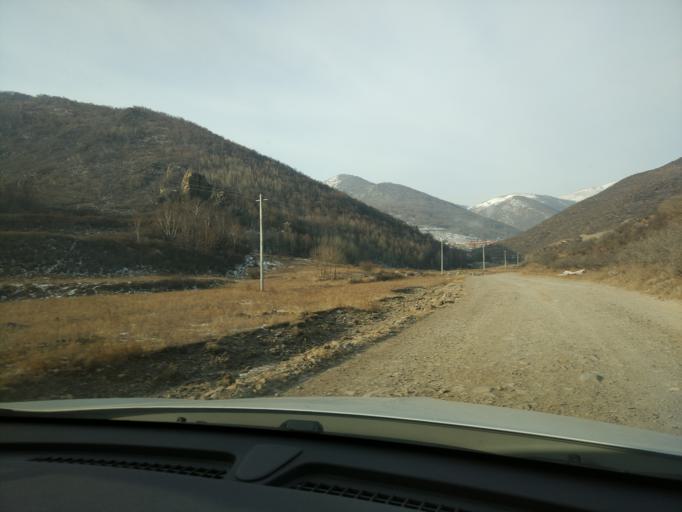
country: CN
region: Hebei
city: Xiwanzi
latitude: 40.8513
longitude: 115.4794
